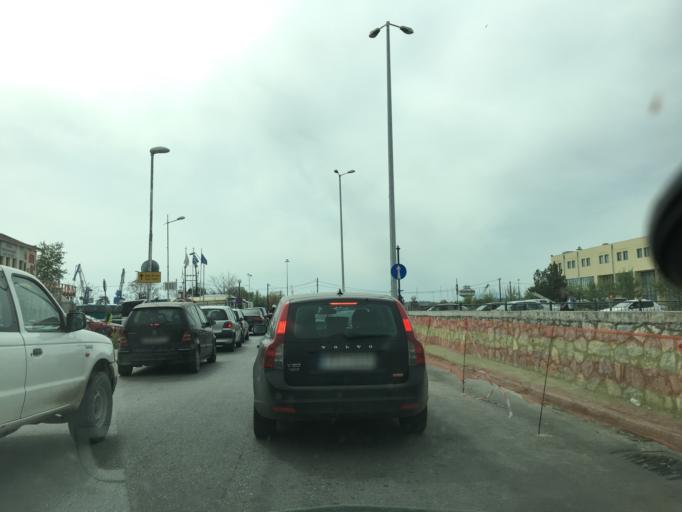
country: GR
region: Thessaly
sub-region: Nomos Magnisias
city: Nea Ionia
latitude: 39.3615
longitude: 22.9323
